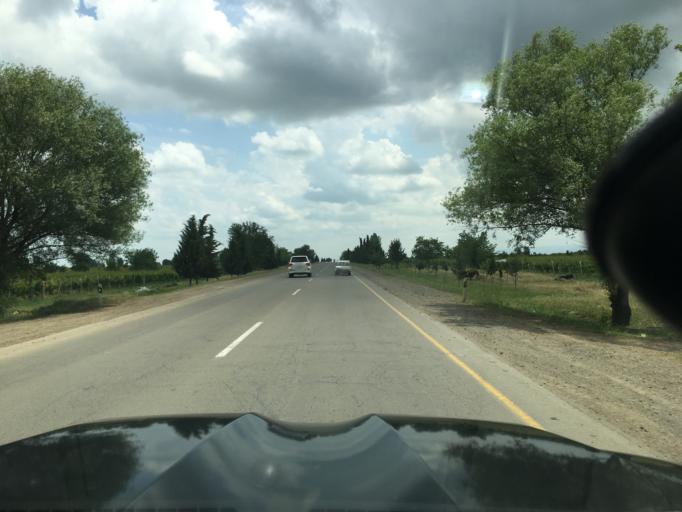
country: AZ
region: Tovuz
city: Tovuz
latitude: 40.9692
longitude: 45.6940
